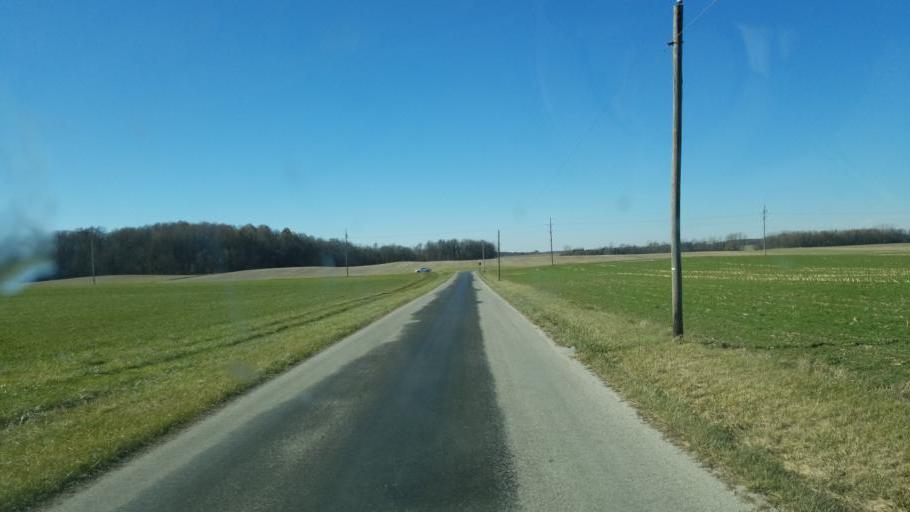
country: US
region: Ohio
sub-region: Huron County
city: Plymouth
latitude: 40.9704
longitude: -82.6932
